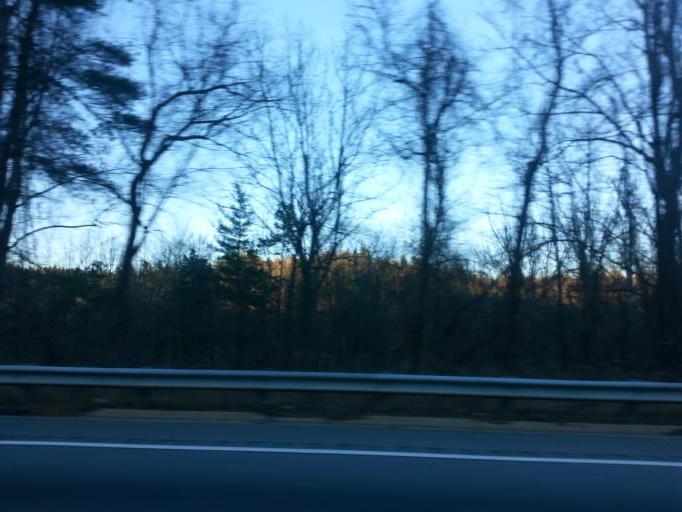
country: US
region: North Carolina
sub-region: Buncombe County
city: Bent Creek
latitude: 35.5096
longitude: -82.5761
